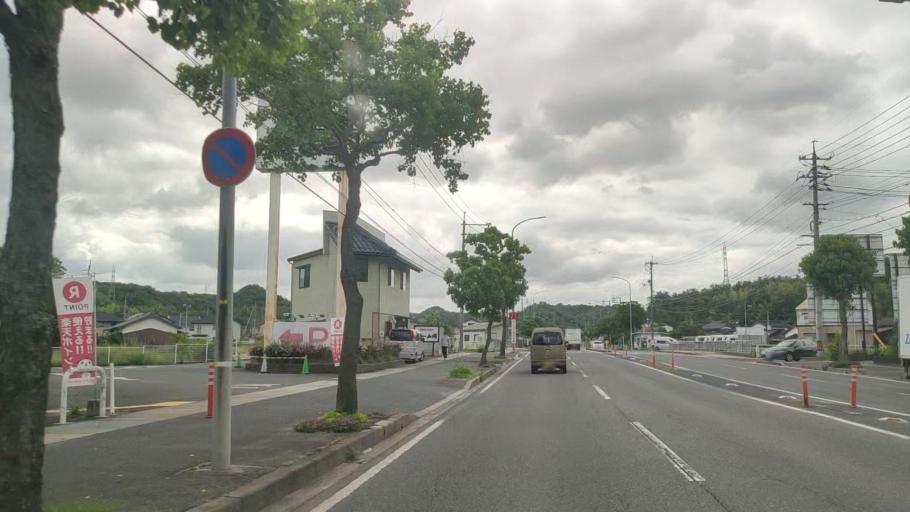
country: JP
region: Tottori
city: Yonago
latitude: 35.4225
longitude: 133.3479
